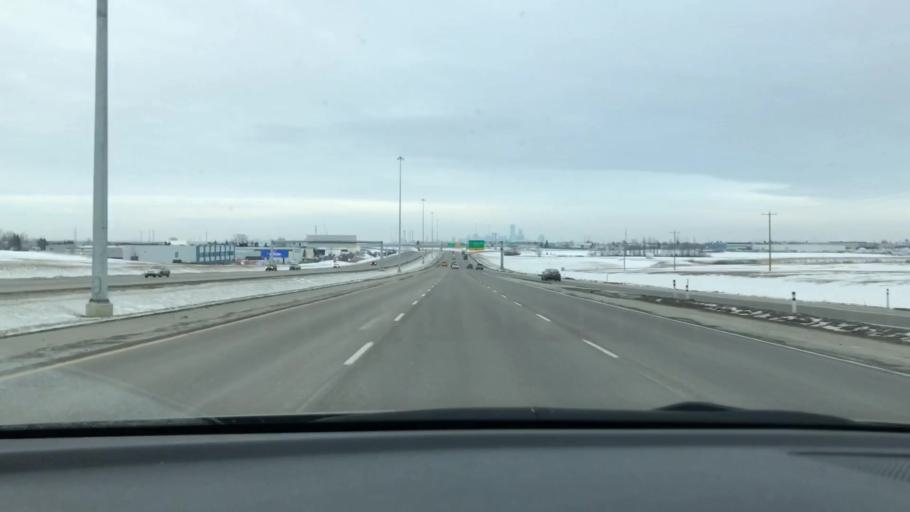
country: CA
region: Alberta
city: Sherwood Park
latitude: 53.5142
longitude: -113.3508
